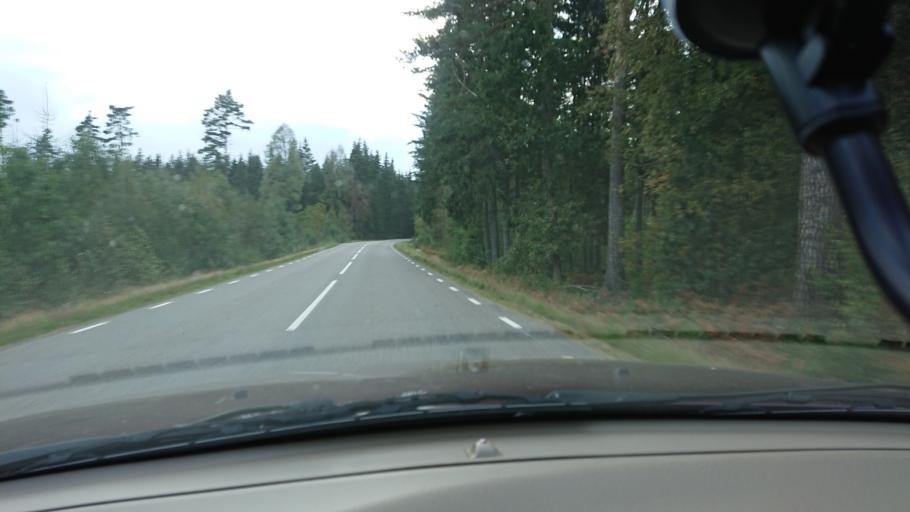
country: SE
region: Kronoberg
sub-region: Vaxjo Kommun
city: Lammhult
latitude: 57.0943
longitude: 14.6869
